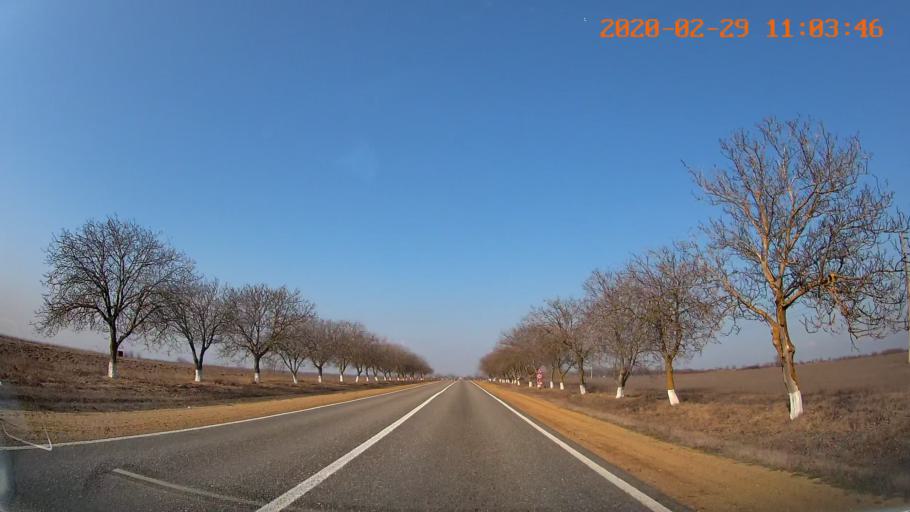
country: MD
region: Criuleni
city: Criuleni
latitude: 47.1817
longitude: 29.2114
